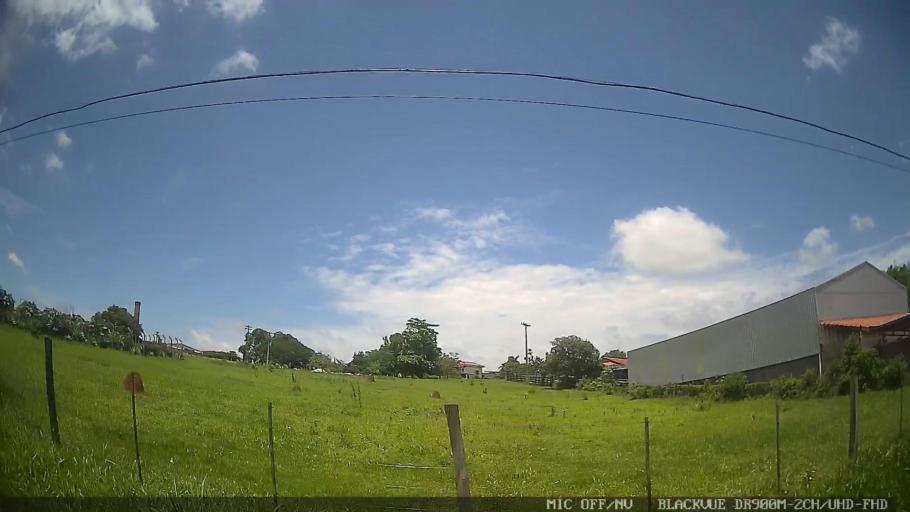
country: BR
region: Sao Paulo
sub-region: Laranjal Paulista
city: Laranjal Paulista
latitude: -23.0372
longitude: -47.8548
